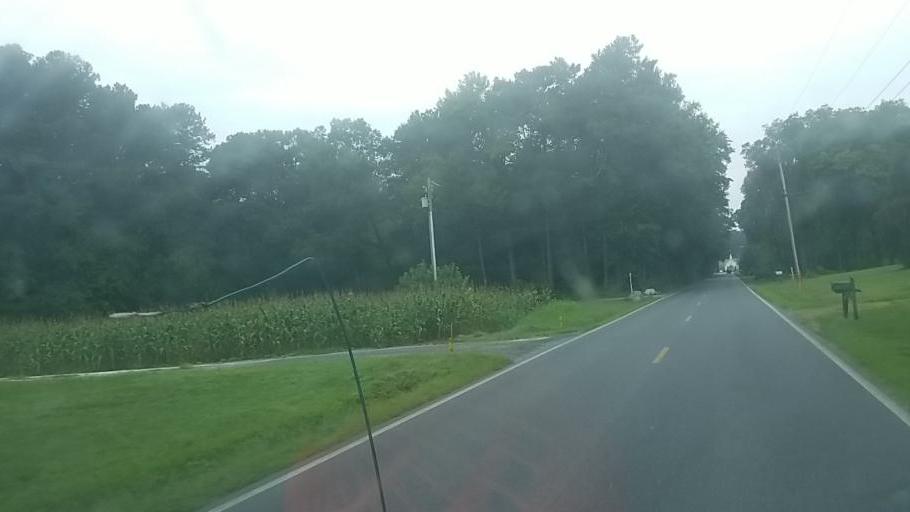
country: US
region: Maryland
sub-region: Wicomico County
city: Delmar
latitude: 38.3958
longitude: -75.5320
